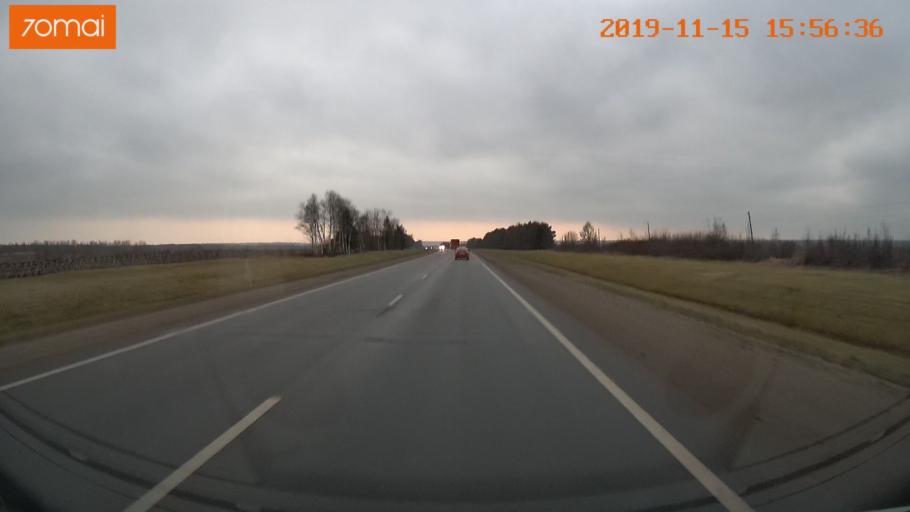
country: RU
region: Jaroslavl
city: Yaroslavl
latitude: 57.8404
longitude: 39.9719
